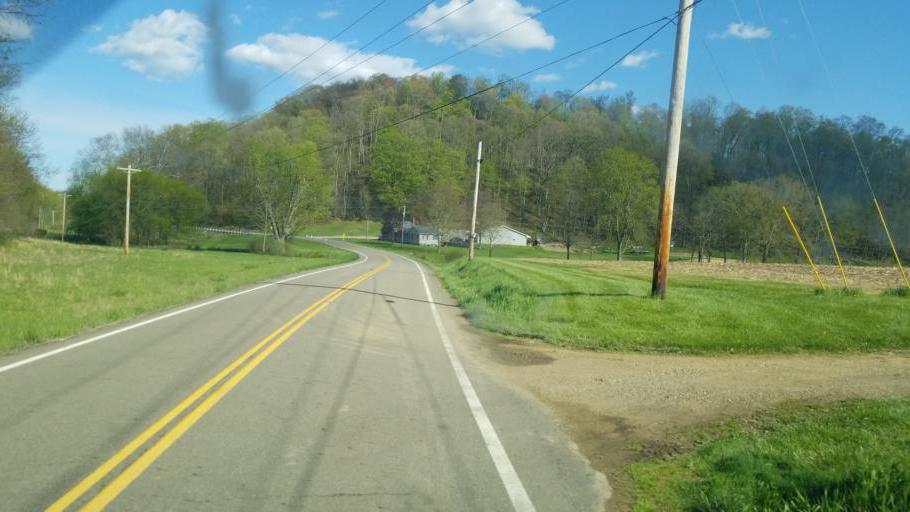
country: US
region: Ohio
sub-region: Coshocton County
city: Coshocton
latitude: 40.3580
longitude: -81.9723
